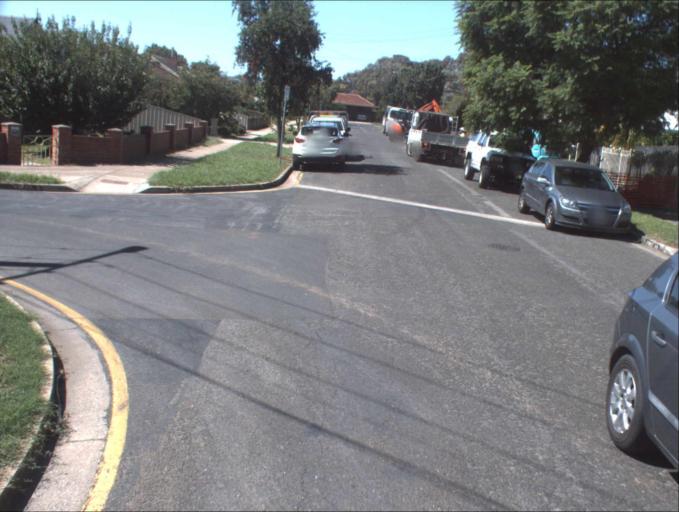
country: AU
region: South Australia
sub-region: Port Adelaide Enfield
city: Klemzig
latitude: -34.8850
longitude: 138.6406
